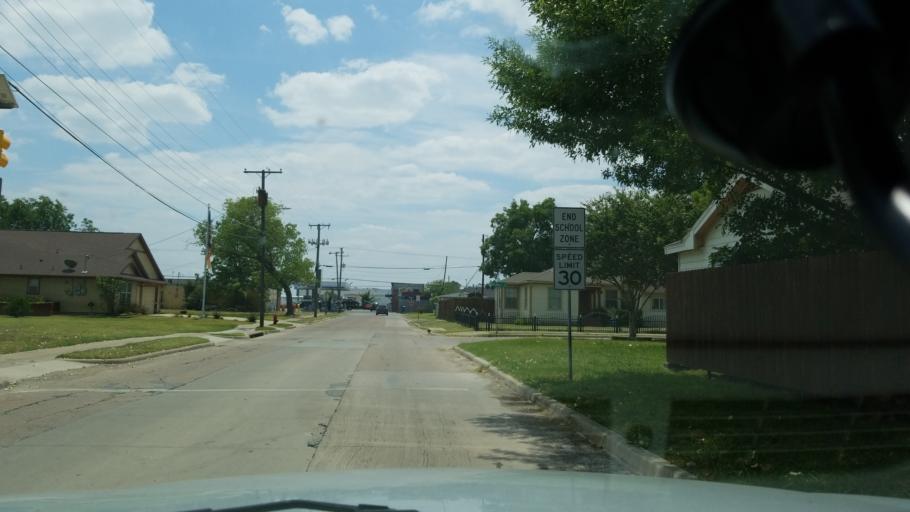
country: US
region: Texas
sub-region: Dallas County
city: Grand Prairie
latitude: 32.7499
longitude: -96.9813
